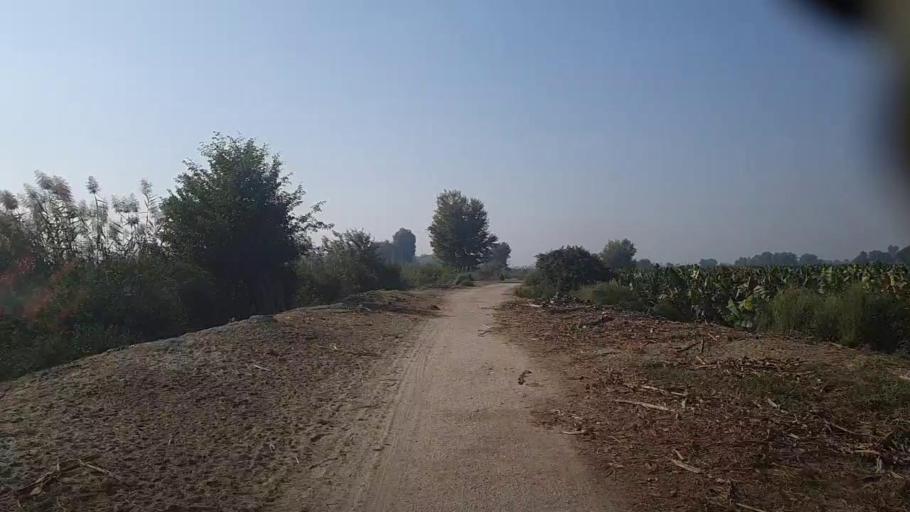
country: PK
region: Sindh
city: Kandiari
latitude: 27.0095
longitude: 68.4987
